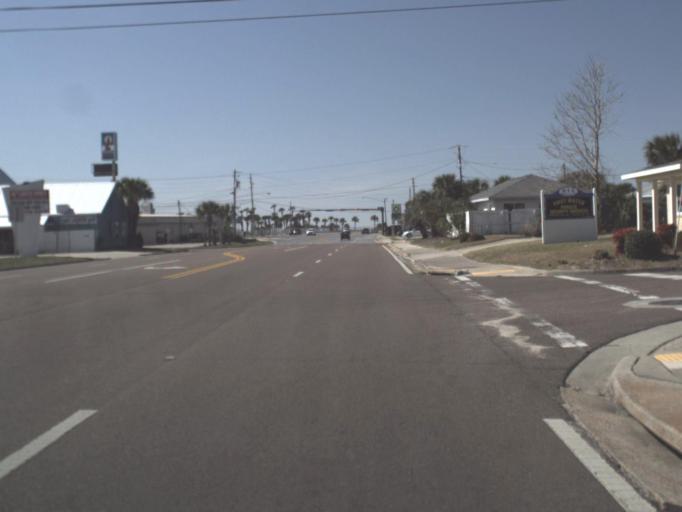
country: US
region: Florida
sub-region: Bay County
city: Panama City Beach
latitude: 30.1991
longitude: -85.8429
